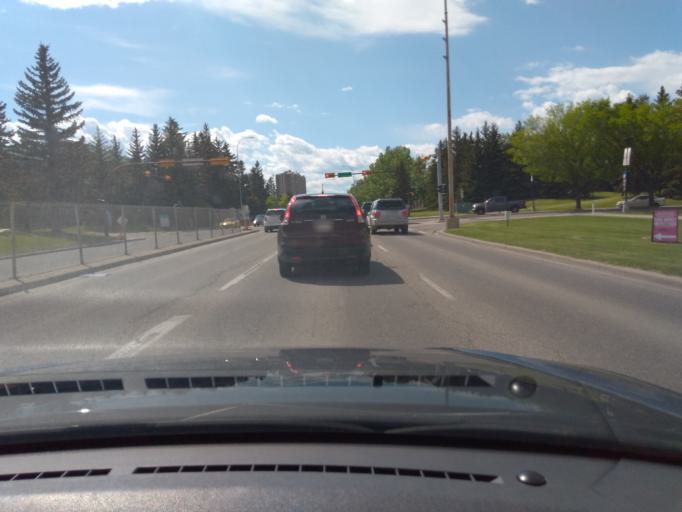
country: CA
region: Alberta
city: Calgary
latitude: 50.9723
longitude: -114.0996
